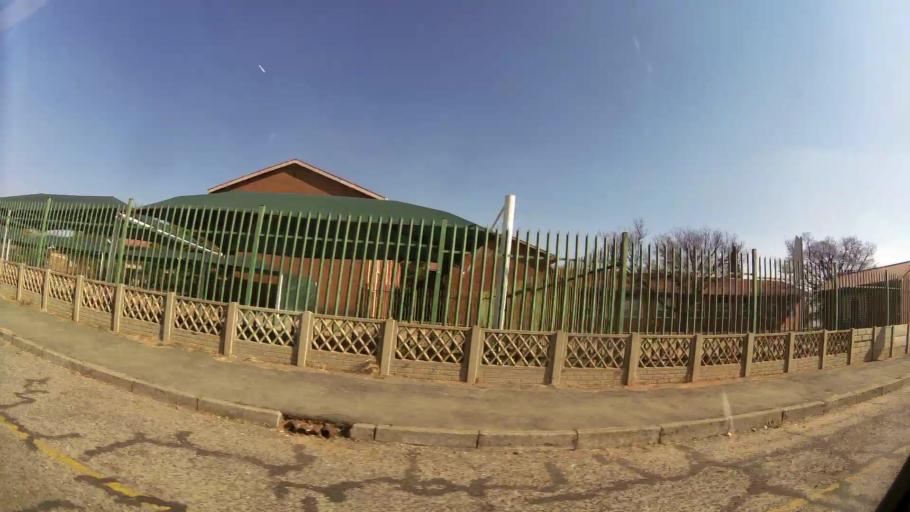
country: ZA
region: Gauteng
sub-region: City of Johannesburg Metropolitan Municipality
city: Johannesburg
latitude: -26.2611
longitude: 28.0208
